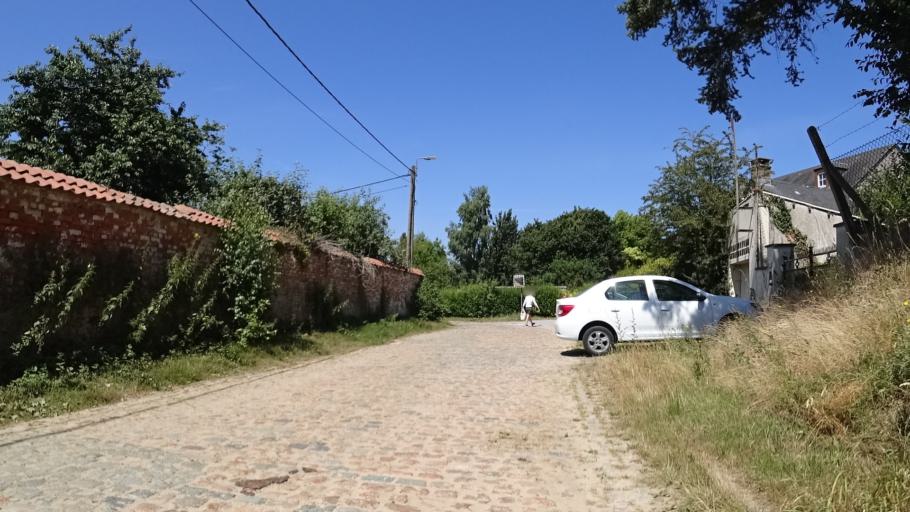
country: BE
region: Wallonia
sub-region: Province du Brabant Wallon
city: Jodoigne
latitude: 50.7163
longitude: 4.8672
